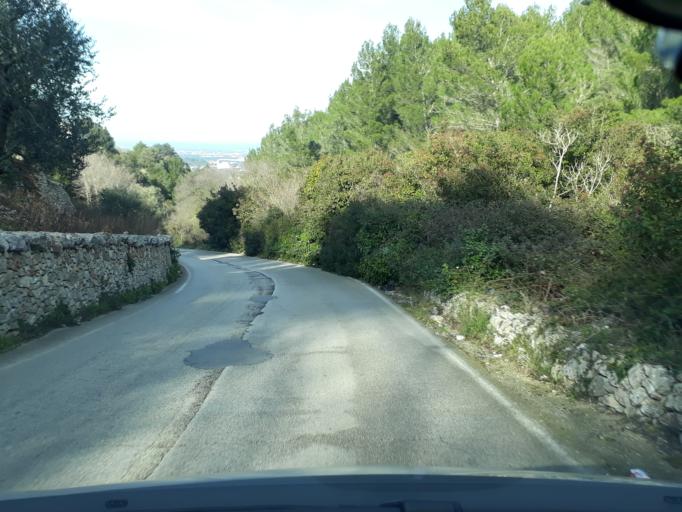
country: IT
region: Apulia
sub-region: Provincia di Brindisi
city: Lamie di Olimpie-Selva
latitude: 40.8026
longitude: 17.3524
